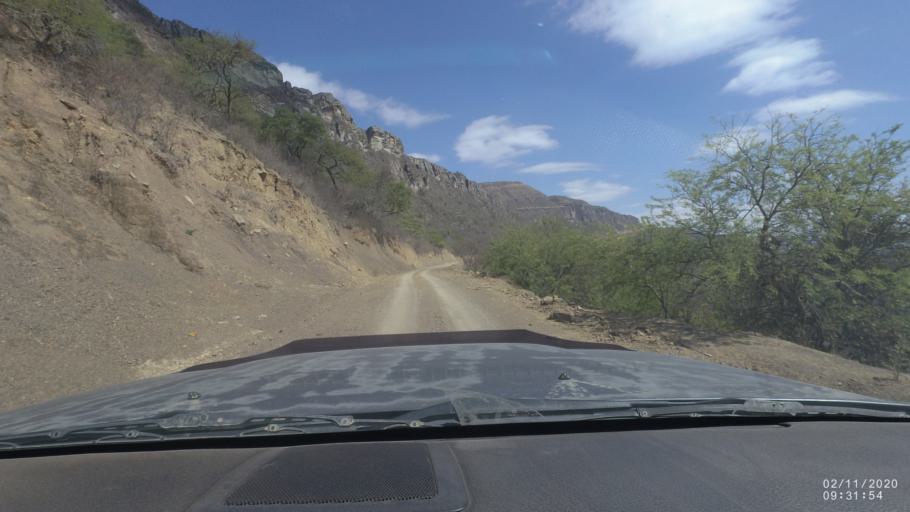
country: BO
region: Chuquisaca
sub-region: Provincia Zudanez
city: Mojocoya
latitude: -18.4246
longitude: -64.5850
